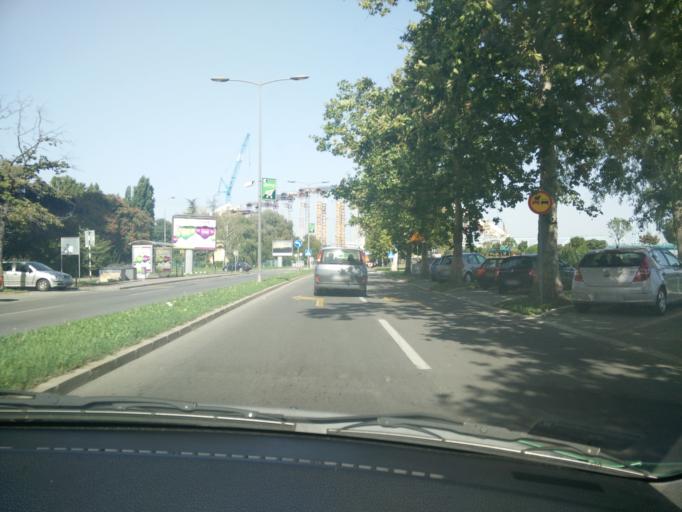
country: RS
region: Autonomna Pokrajina Vojvodina
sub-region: Juznobacki Okrug
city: Novi Sad
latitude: 45.2604
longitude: 19.8557
